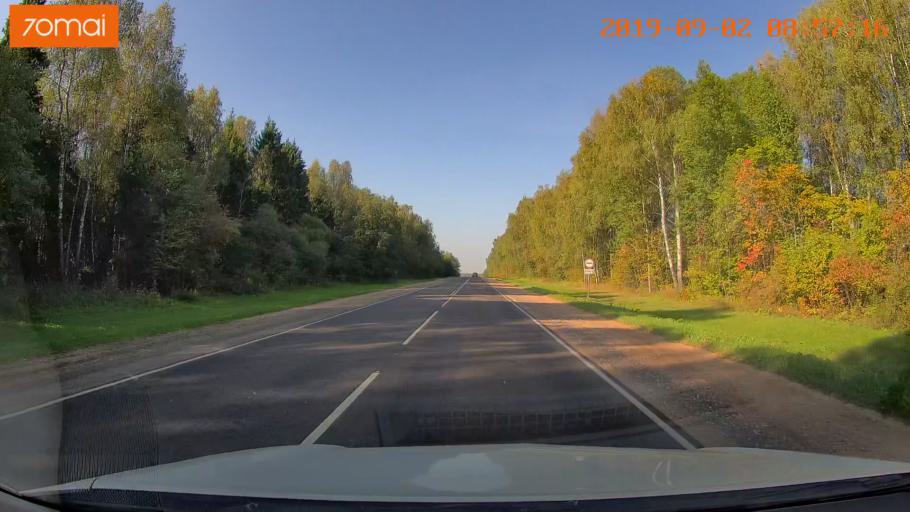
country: RU
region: Kaluga
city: Medyn'
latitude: 54.9383
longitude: 35.7723
